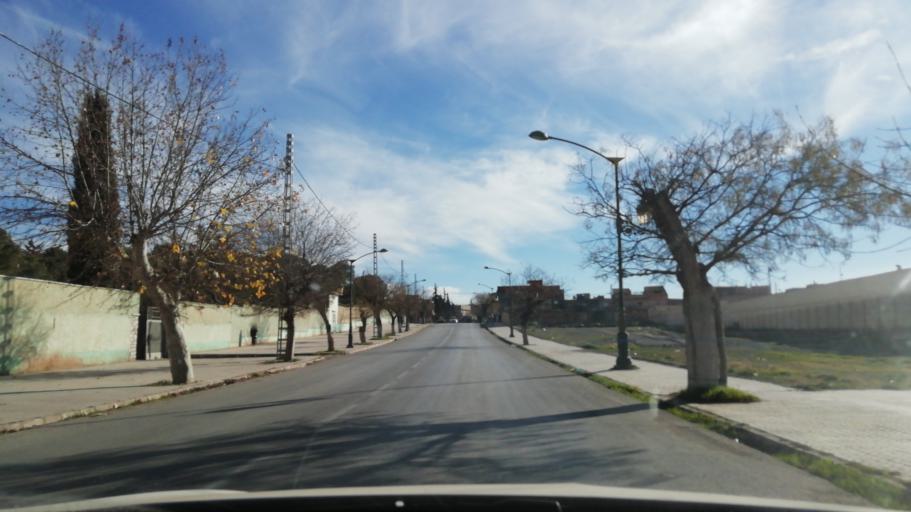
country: DZ
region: Tlemcen
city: Sebdou
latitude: 34.6352
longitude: -1.3335
